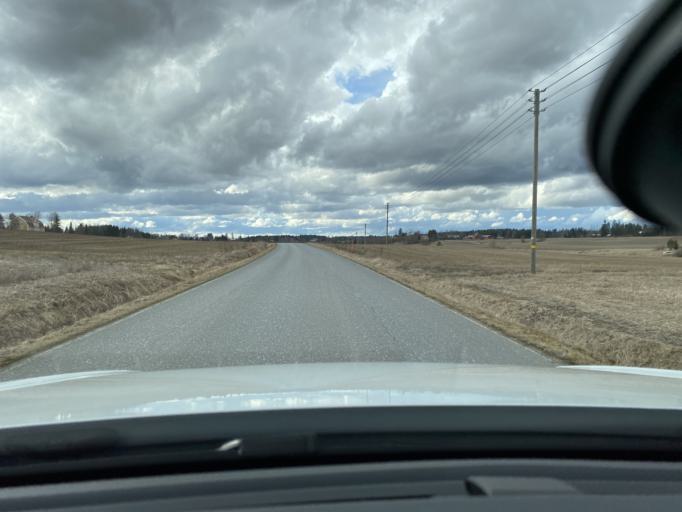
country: FI
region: Pirkanmaa
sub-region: Lounais-Pirkanmaa
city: Punkalaidun
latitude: 61.1164
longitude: 23.0719
